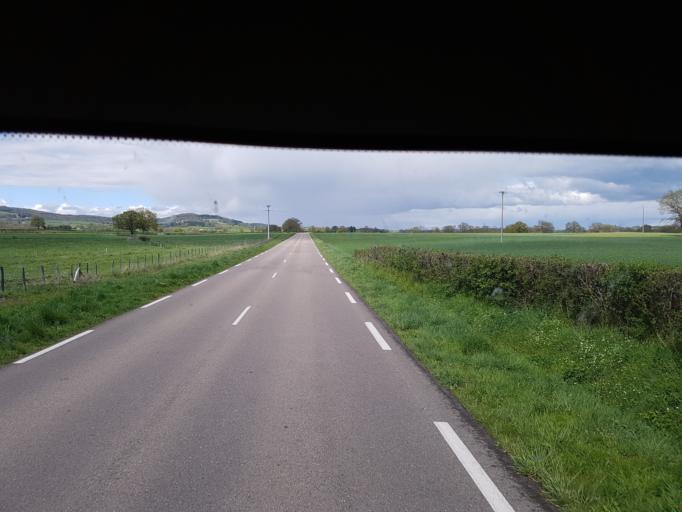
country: FR
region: Bourgogne
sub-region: Departement de Saone-et-Loire
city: Etang-sur-Arroux
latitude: 46.8943
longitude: 4.1886
